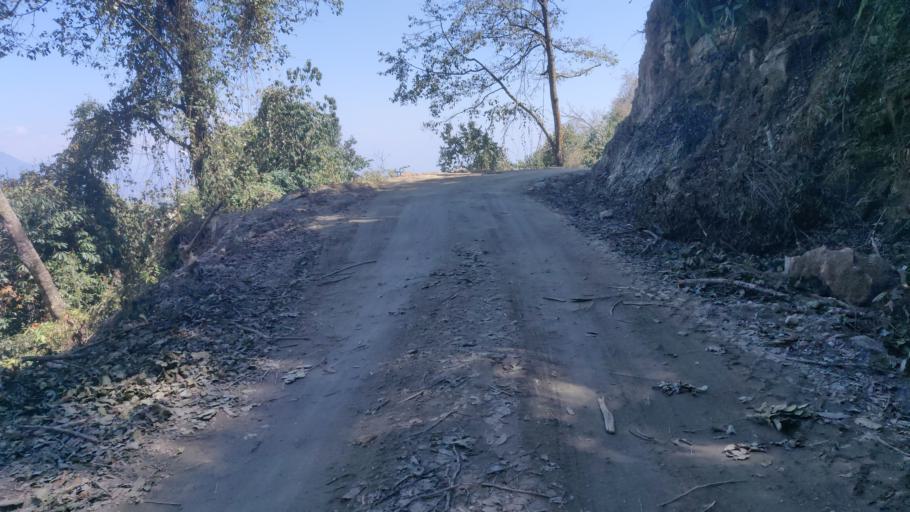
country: NP
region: Central Region
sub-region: Bagmati Zone
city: Nagarkot
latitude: 27.7837
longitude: 85.4820
